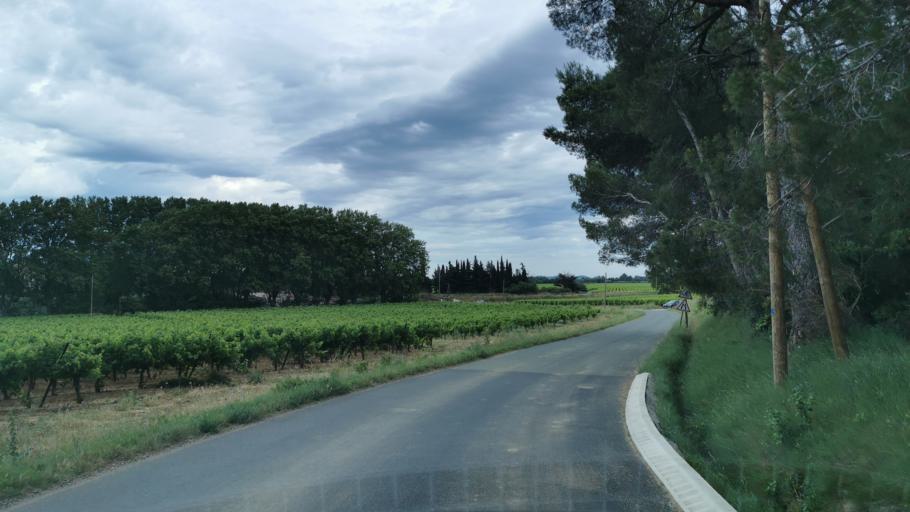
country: FR
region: Languedoc-Roussillon
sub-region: Departement de l'Aude
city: Moussan
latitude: 43.2427
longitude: 2.9660
